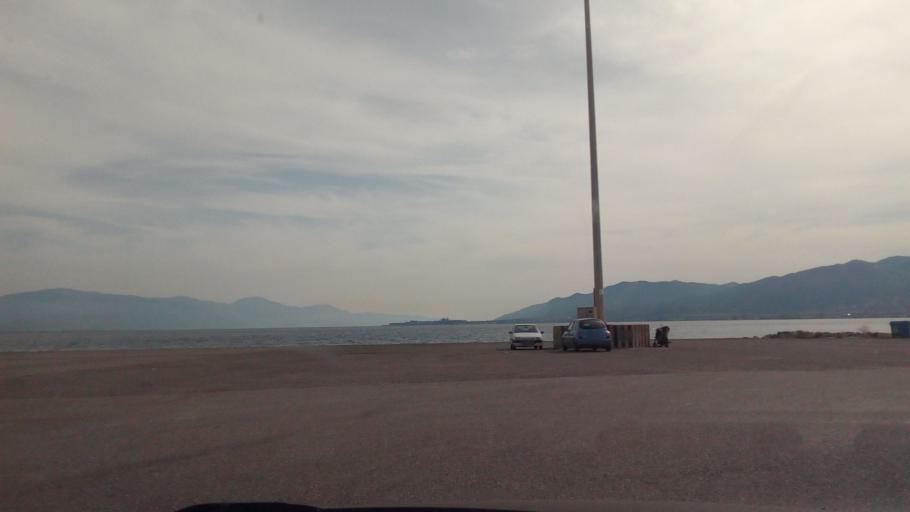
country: GR
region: West Greece
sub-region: Nomos Aitolias kai Akarnanias
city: Antirrio
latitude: 38.3318
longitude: 21.7681
